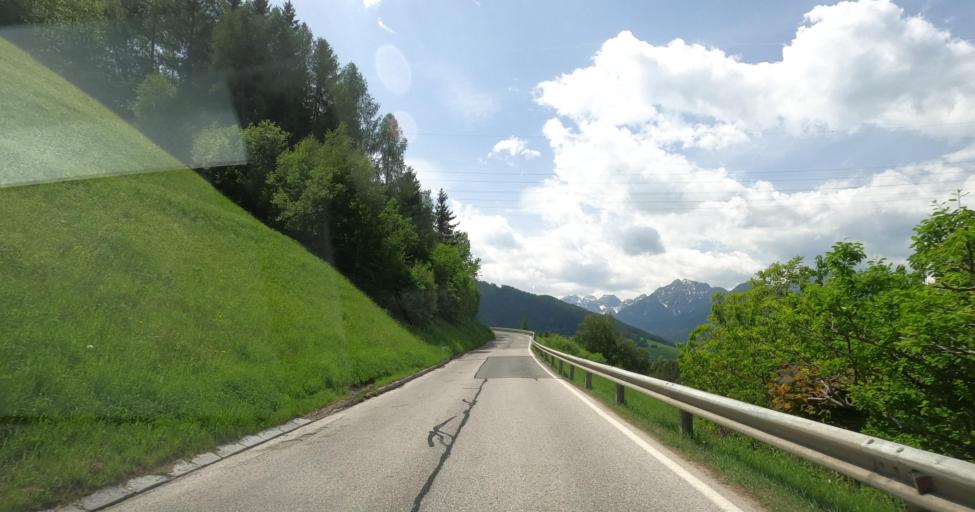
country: AT
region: Tyrol
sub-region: Politischer Bezirk Innsbruck Land
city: Schoenberg im Stubaital
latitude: 47.1843
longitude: 11.4359
